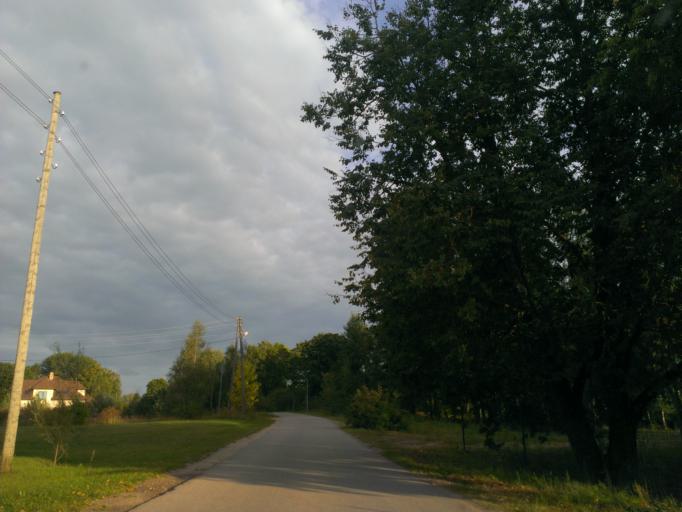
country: LV
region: Ikskile
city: Ikskile
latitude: 56.8409
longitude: 24.5044
